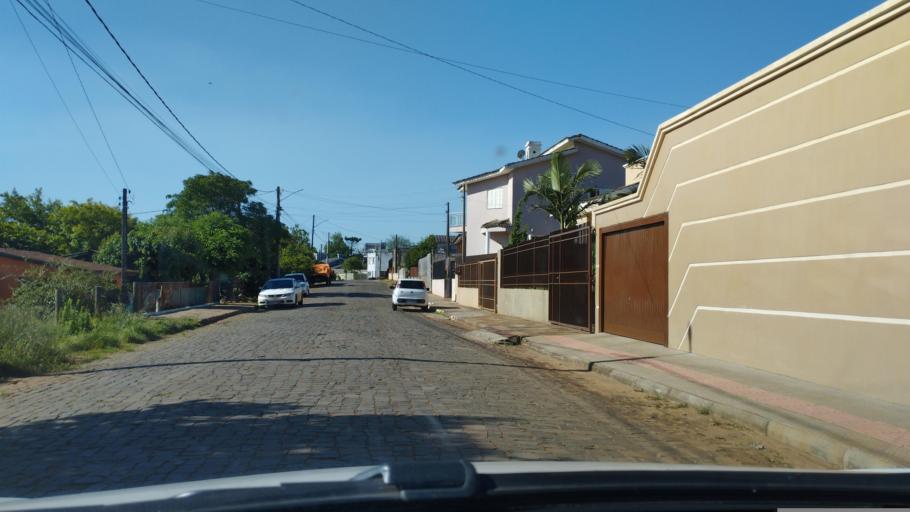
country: BR
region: Rio Grande do Sul
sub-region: Tupancireta
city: Tupancireta
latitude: -29.0843
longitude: -53.8383
